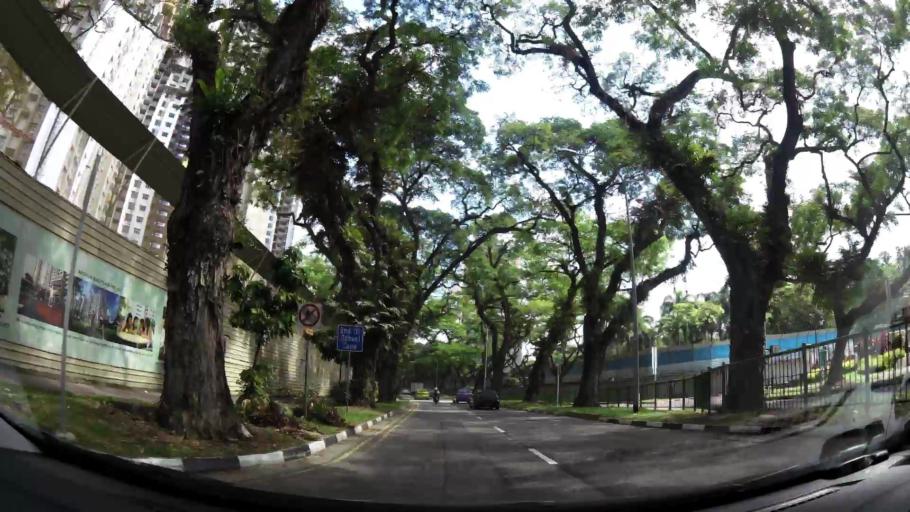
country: SG
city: Singapore
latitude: 1.2860
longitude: 103.8217
